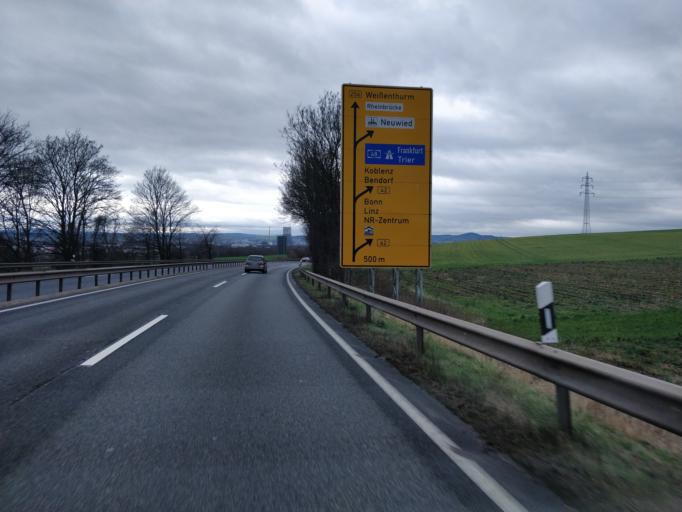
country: DE
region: Rheinland-Pfalz
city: Neuwied
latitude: 50.4495
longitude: 7.4865
